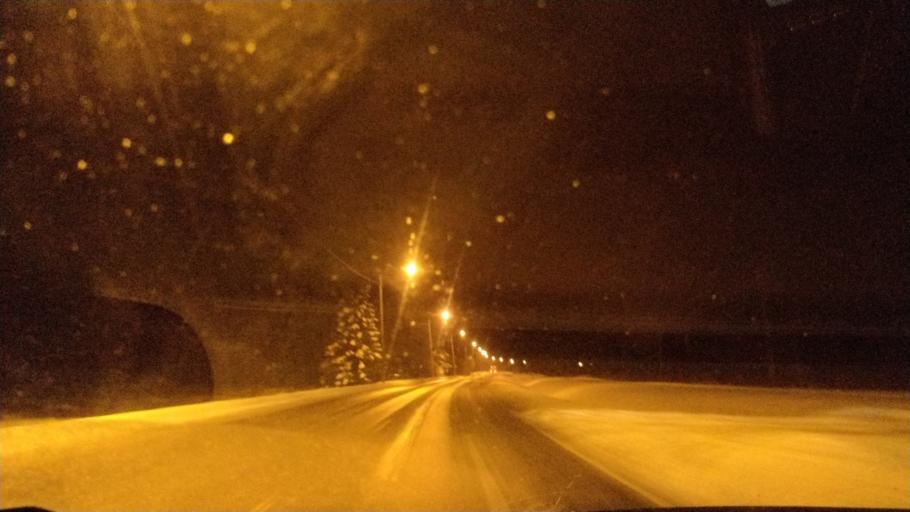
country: FI
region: Lapland
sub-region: Rovaniemi
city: Rovaniemi
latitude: 66.3157
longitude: 25.3618
